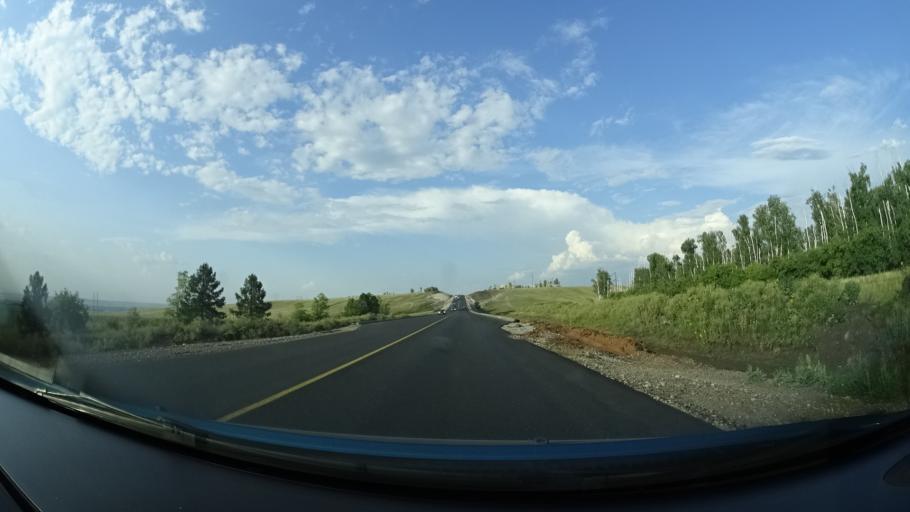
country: RU
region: Samara
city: Sukhodol
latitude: 53.7282
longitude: 50.8377
